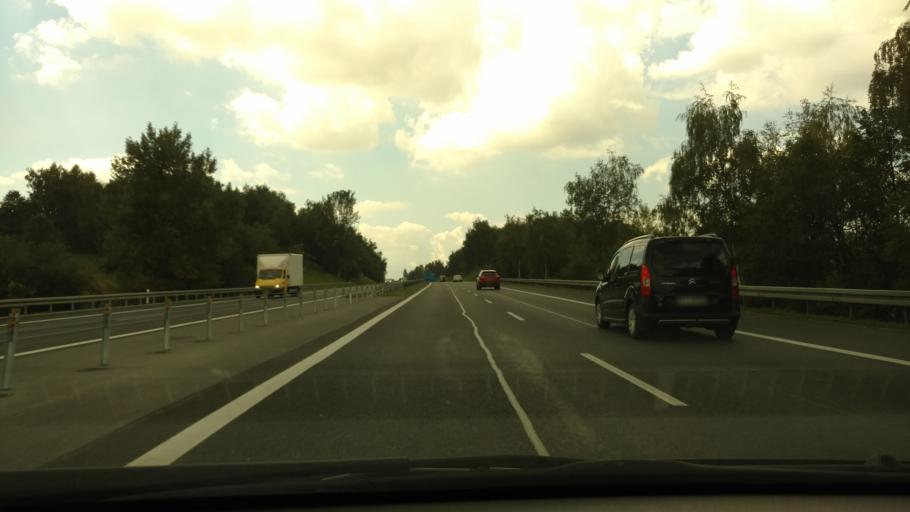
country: PL
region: Lesser Poland Voivodeship
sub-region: Powiat krakowski
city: Rzaska
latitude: 50.0998
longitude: 19.8287
